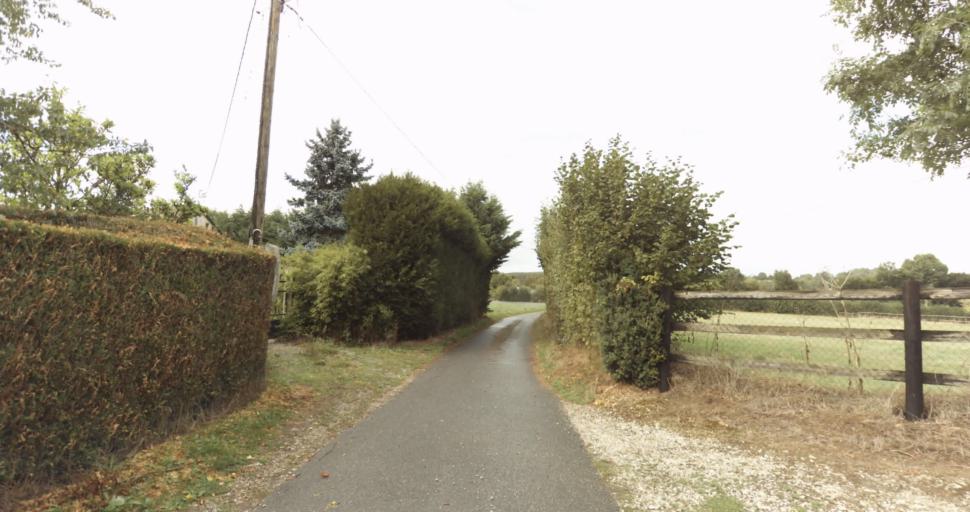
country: FR
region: Lower Normandy
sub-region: Departement de l'Orne
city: Sainte-Gauburge-Sainte-Colombe
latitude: 48.7051
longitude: 0.3810
